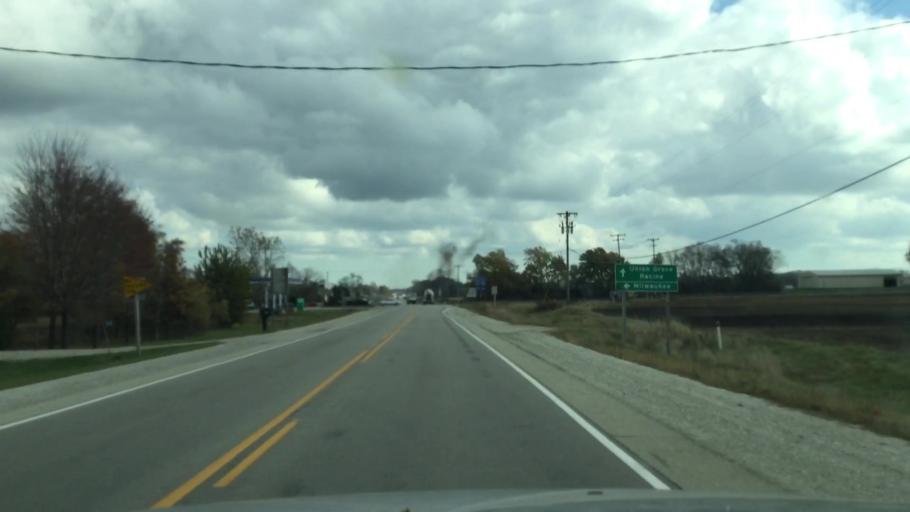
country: US
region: Wisconsin
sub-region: Racine County
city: Union Grove
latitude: 42.7422
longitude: -88.0740
